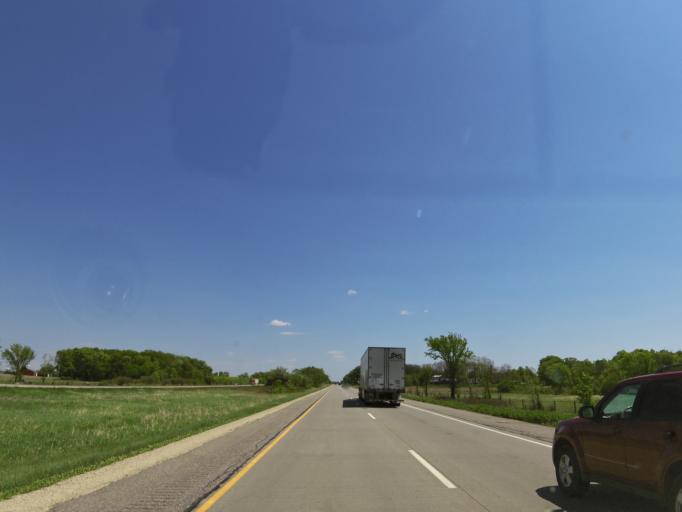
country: US
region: Wisconsin
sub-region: Juneau County
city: New Lisbon
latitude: 43.9012
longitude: -90.1962
